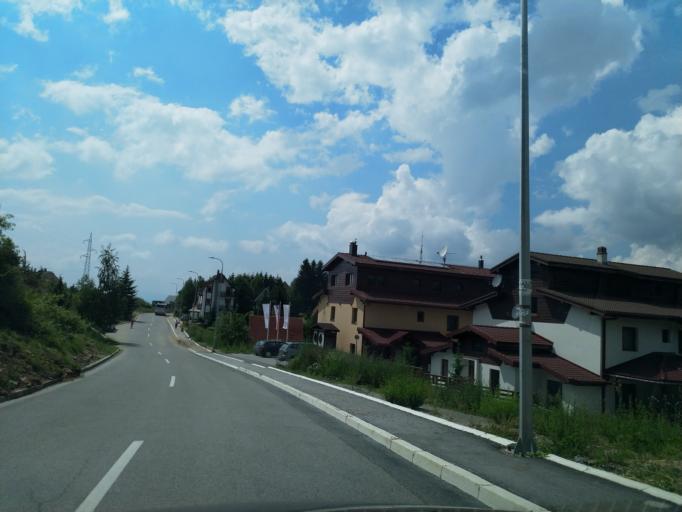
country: RS
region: Central Serbia
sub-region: Raski Okrug
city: Raska
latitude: 43.2734
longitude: 20.7709
